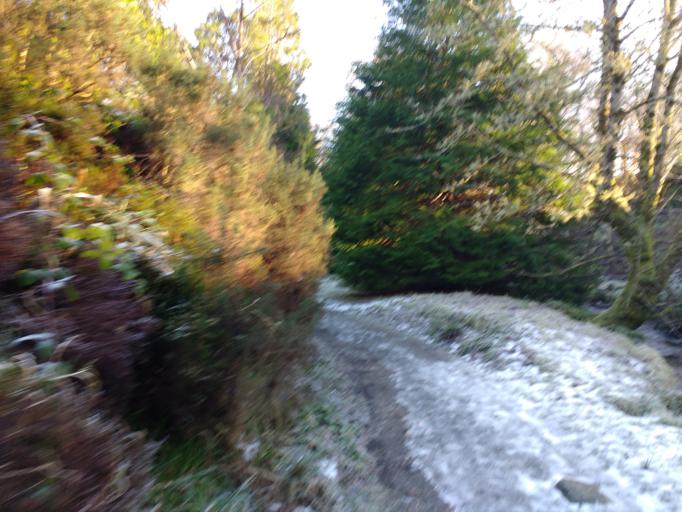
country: GB
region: Scotland
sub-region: Eilean Siar
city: Isle of Lewis
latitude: 58.2191
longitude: -6.3958
